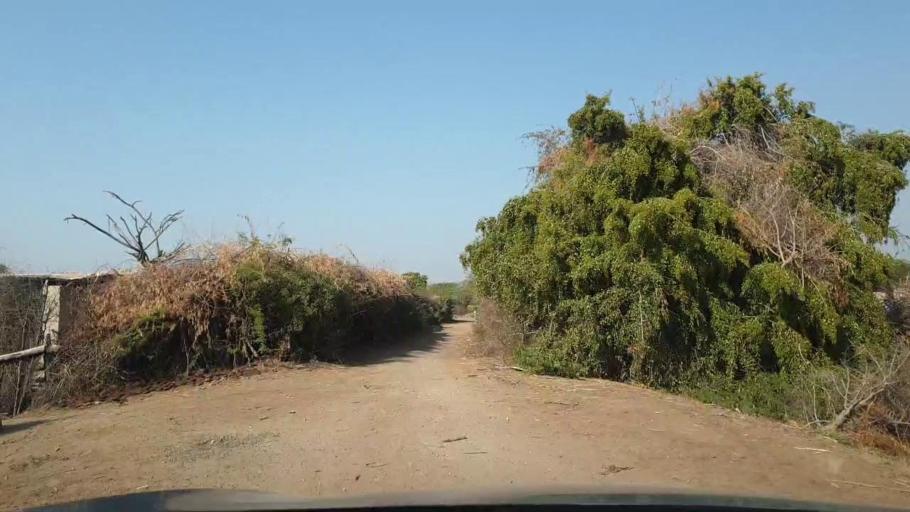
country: PK
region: Sindh
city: Berani
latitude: 25.6276
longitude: 68.8454
